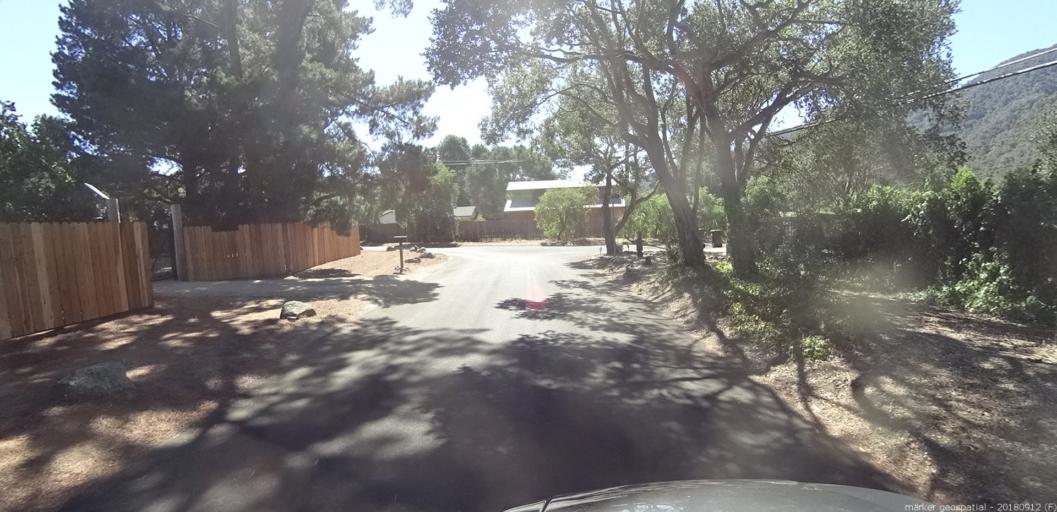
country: US
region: California
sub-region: Monterey County
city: Carmel Valley Village
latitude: 36.4879
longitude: -121.7450
